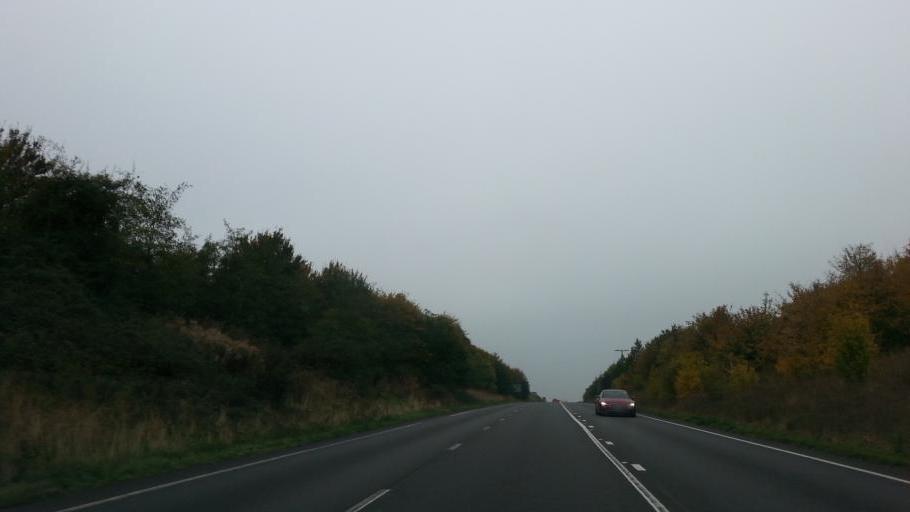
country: GB
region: England
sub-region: Peterborough
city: Castor
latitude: 52.5247
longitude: -0.3664
